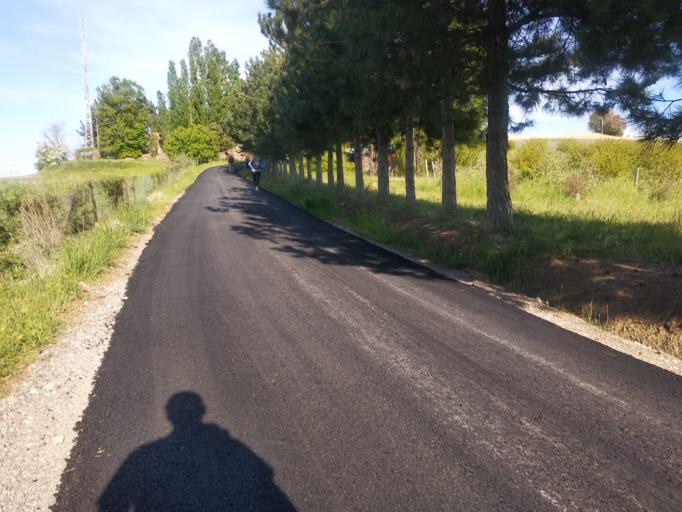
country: IT
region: Emilia-Romagna
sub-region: Provincia di Ravenna
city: Fognano
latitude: 44.2244
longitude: 11.7314
